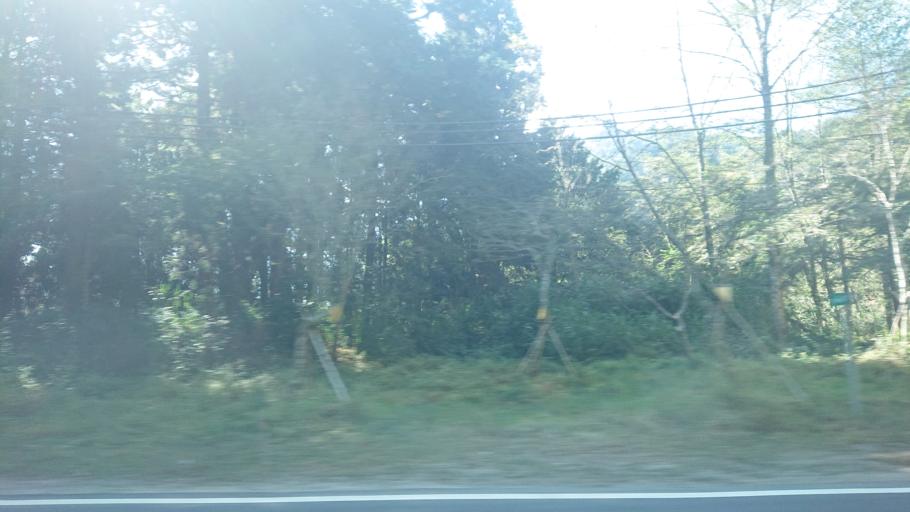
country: TW
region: Taiwan
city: Lugu
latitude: 23.5055
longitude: 120.8195
